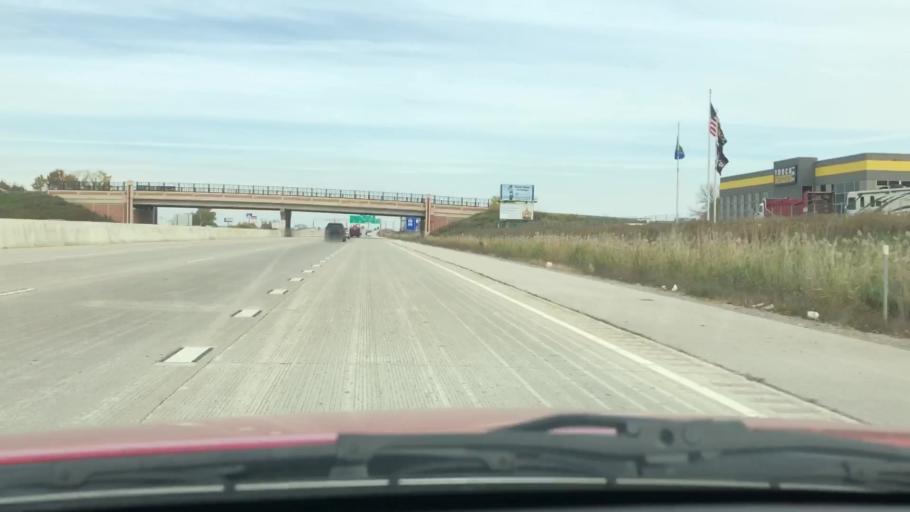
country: US
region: Wisconsin
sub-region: Brown County
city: De Pere
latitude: 44.4586
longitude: -88.0856
